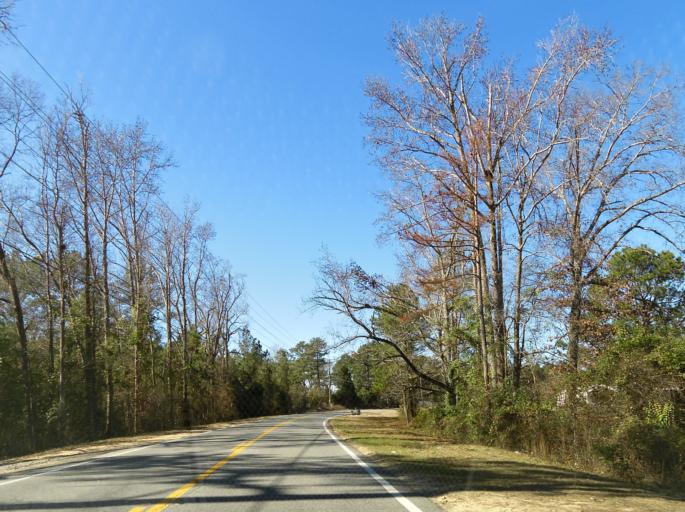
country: US
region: Georgia
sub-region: Bibb County
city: West Point
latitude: 32.7584
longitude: -83.7653
